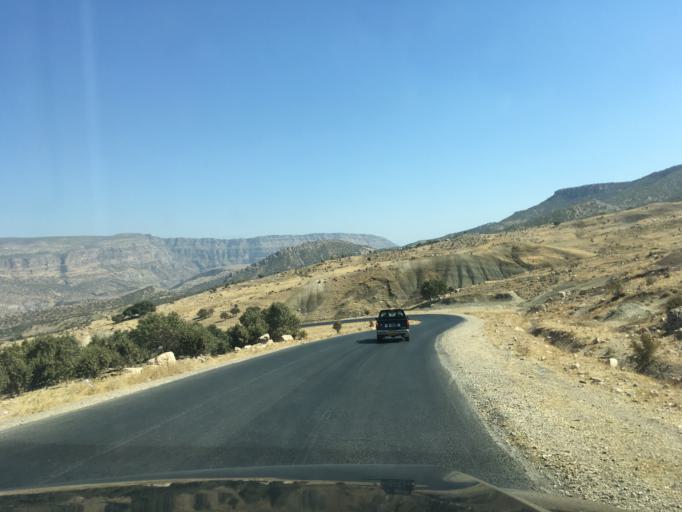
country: IQ
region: Arbil
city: Ruwandiz
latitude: 36.6435
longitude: 44.3417
